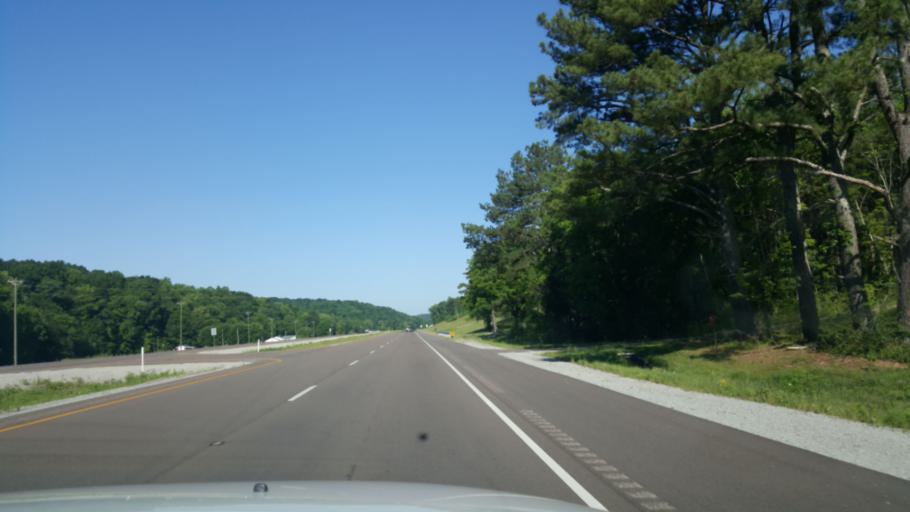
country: US
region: Tennessee
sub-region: Wayne County
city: Waynesboro
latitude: 35.2966
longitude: -87.8176
